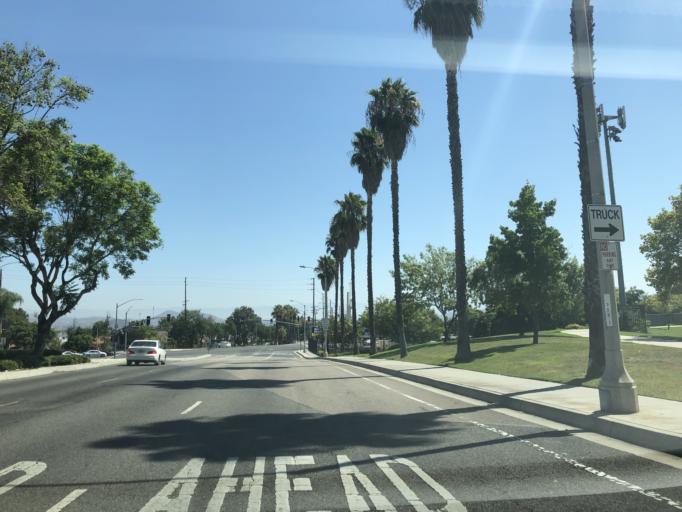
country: US
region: California
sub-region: Riverside County
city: Corona
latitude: 33.8540
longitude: -117.5624
